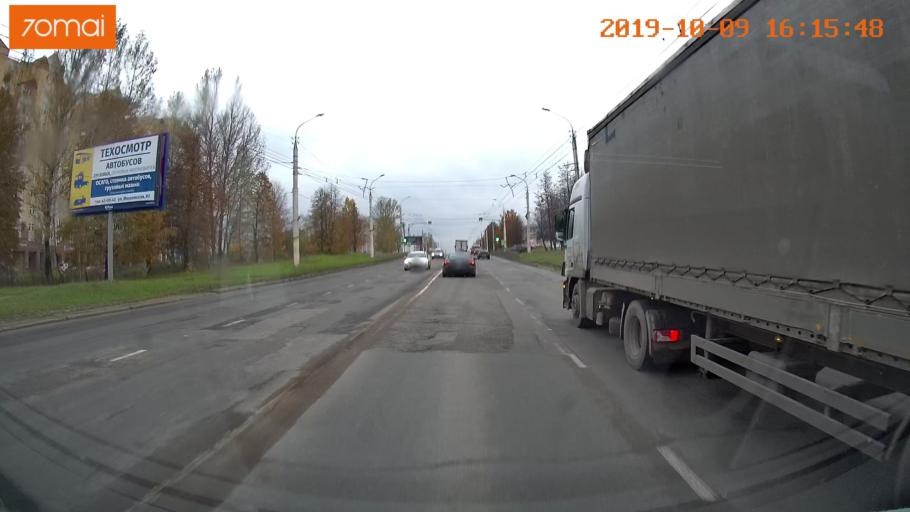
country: RU
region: Kostroma
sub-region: Kostromskoy Rayon
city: Kostroma
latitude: 57.7384
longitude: 40.9139
